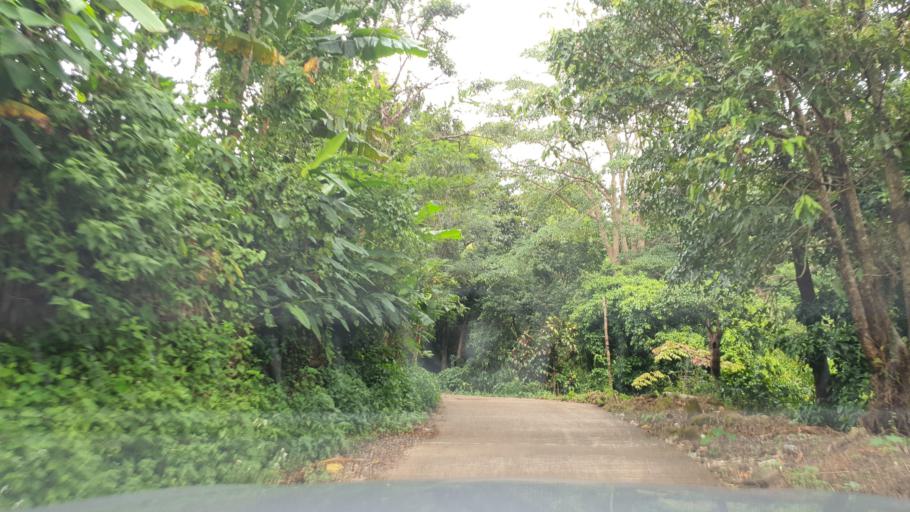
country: TH
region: Chiang Mai
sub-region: Amphoe Chiang Dao
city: Chiang Dao
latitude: 19.2569
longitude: 98.9212
